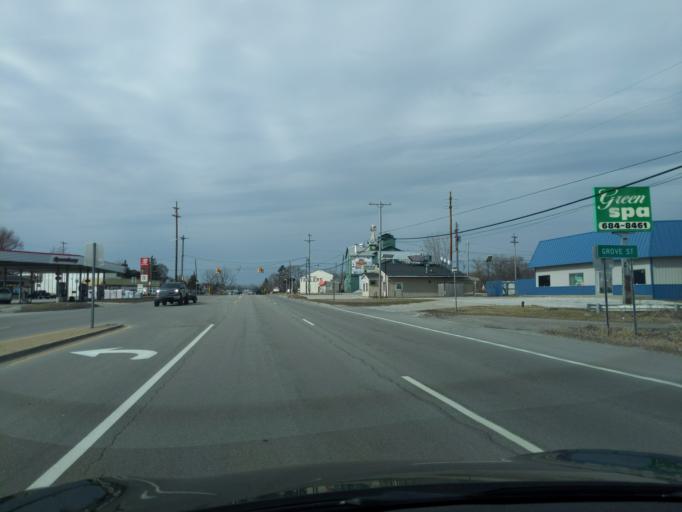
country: US
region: Michigan
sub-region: Bay County
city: Bay City
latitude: 43.6508
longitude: -83.9424
